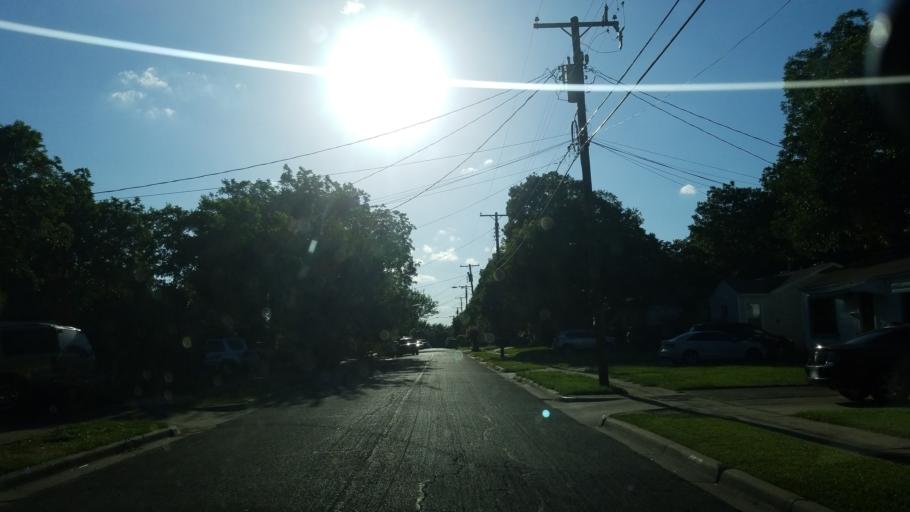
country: US
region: Texas
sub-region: Dallas County
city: Balch Springs
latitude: 32.7752
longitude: -96.7072
